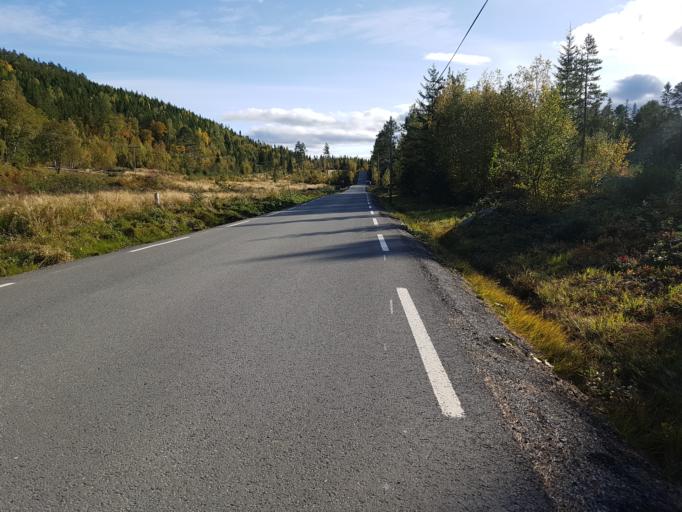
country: NO
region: Sor-Trondelag
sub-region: Malvik
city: Malvik
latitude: 63.3734
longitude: 10.6121
